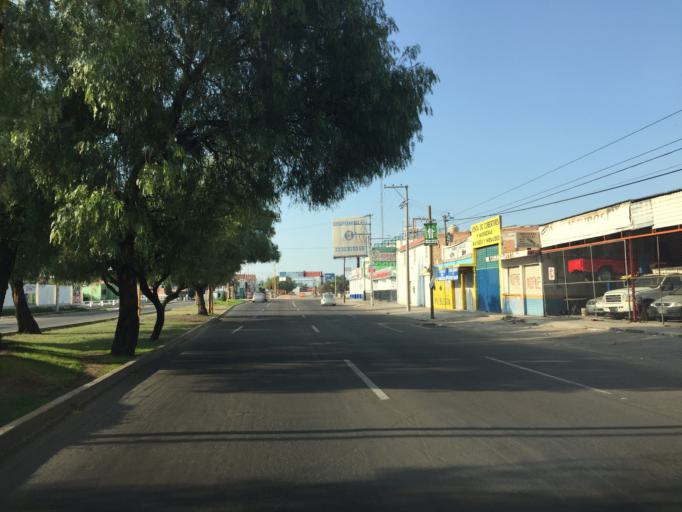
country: MX
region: Aguascalientes
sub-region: Aguascalientes
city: La Loma de los Negritos
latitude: 21.8666
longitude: -102.3179
